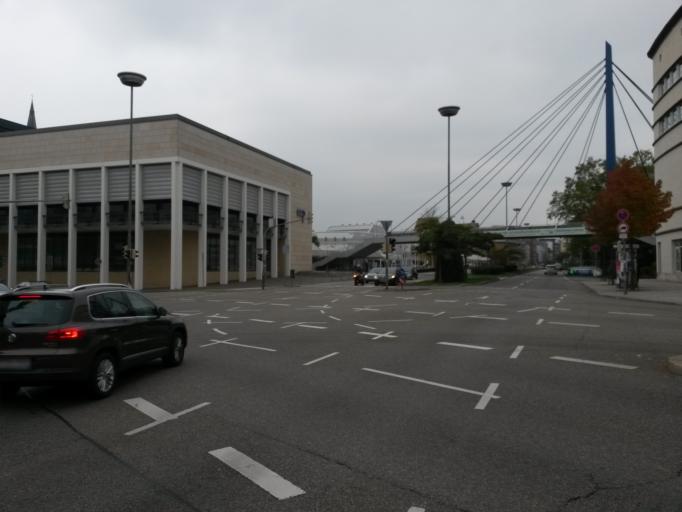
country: DE
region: Baden-Wuerttemberg
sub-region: Karlsruhe Region
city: Pforzheim
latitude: 48.8900
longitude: 8.7040
